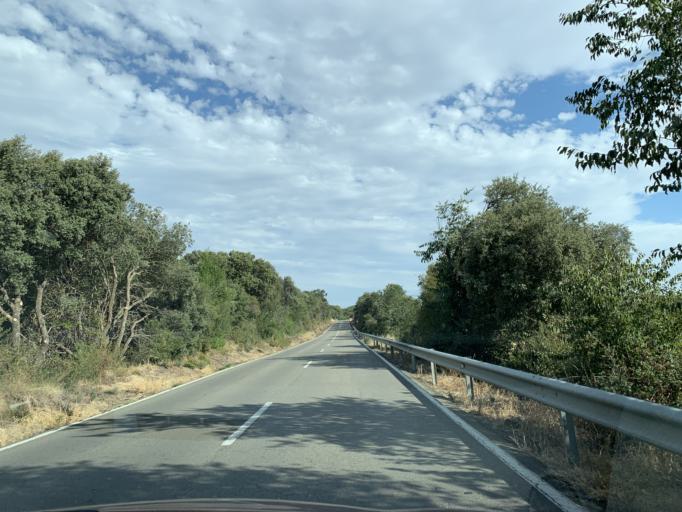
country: ES
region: Aragon
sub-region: Provincia de Zaragoza
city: Santa Eulalia de Gallego
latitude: 42.3085
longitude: -0.7480
